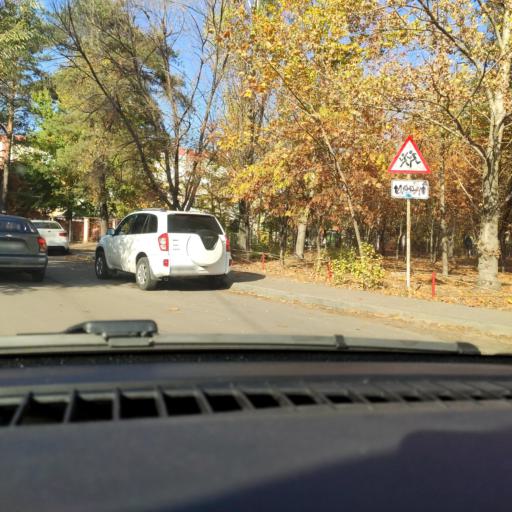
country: RU
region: Voronezj
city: Podgornoye
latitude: 51.7194
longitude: 39.1711
